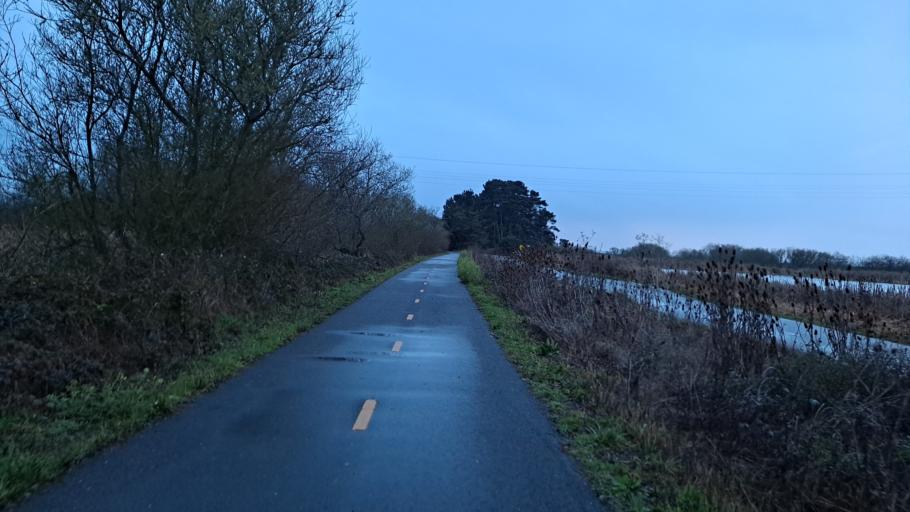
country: US
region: California
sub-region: Humboldt County
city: Arcata
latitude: 40.8602
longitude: -124.0937
